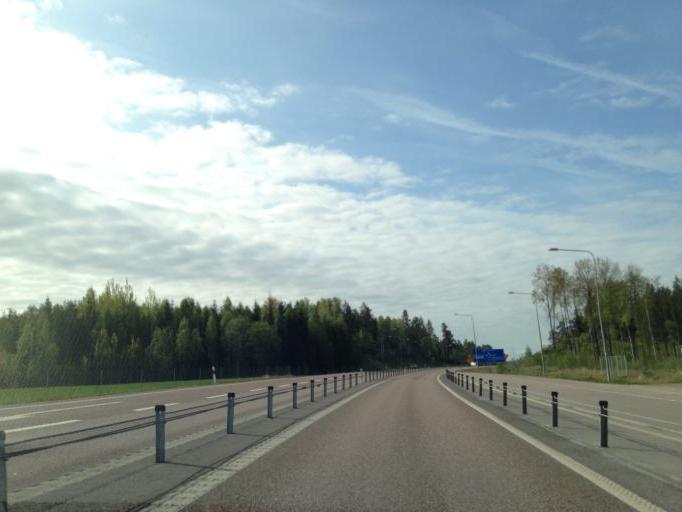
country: SE
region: Soedermanland
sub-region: Flens Kommun
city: Malmkoping
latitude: 59.1432
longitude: 16.7124
